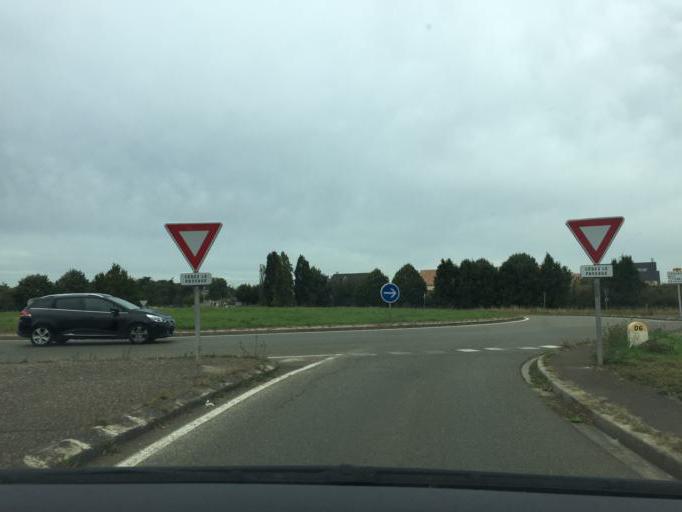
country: FR
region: Ile-de-France
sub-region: Departement de l'Essonne
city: Villiers-le-Bacle
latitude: 48.7422
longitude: 2.1200
